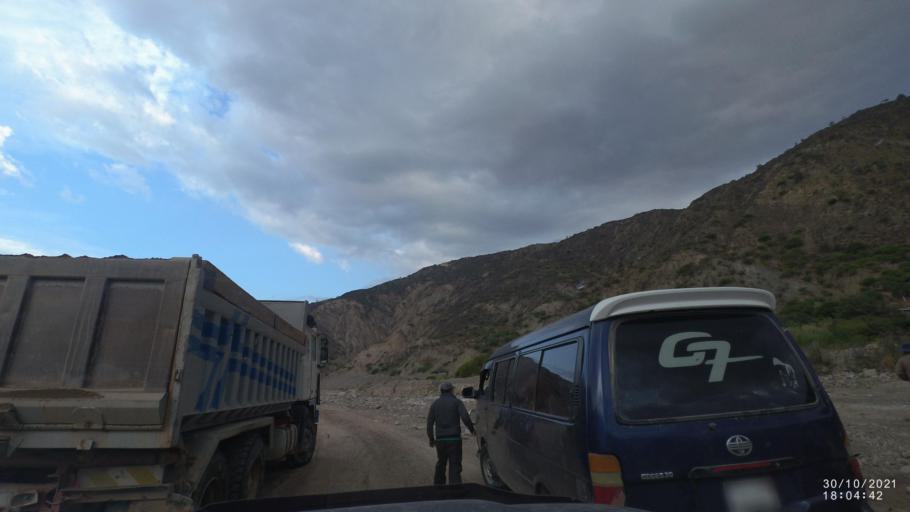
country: BO
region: Cochabamba
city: Sipe Sipe
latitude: -17.5598
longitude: -66.4606
